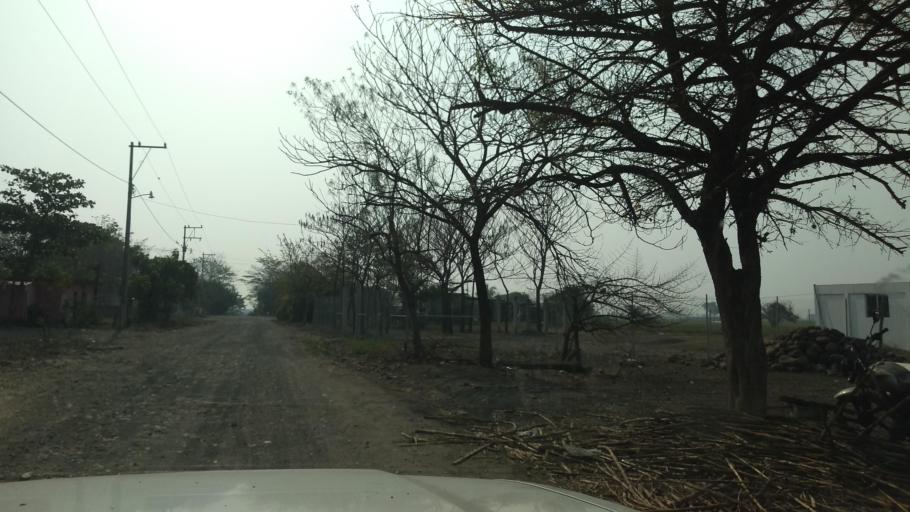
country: MX
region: Oaxaca
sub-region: Cosolapa
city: Cosolapa
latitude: 18.6226
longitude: -96.6025
